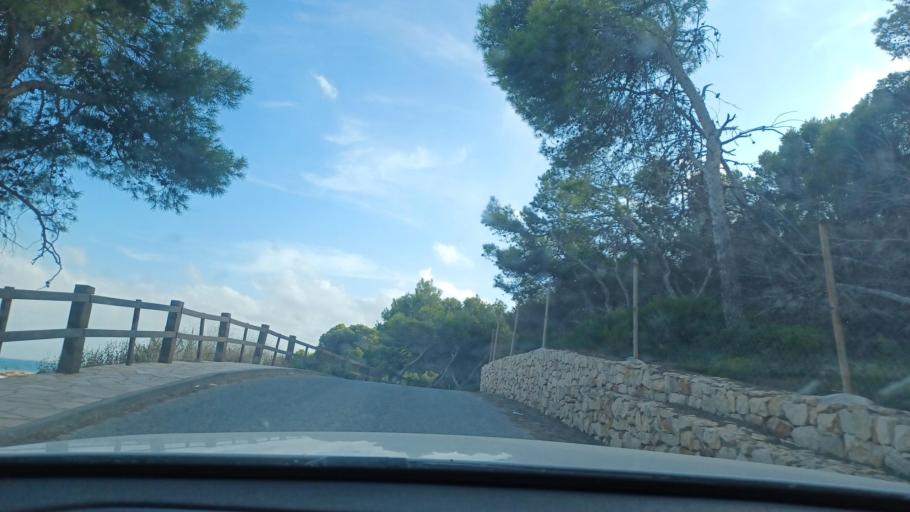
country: ES
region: Catalonia
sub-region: Provincia de Tarragona
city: L'Ampolla
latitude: 40.8300
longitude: 0.7412
